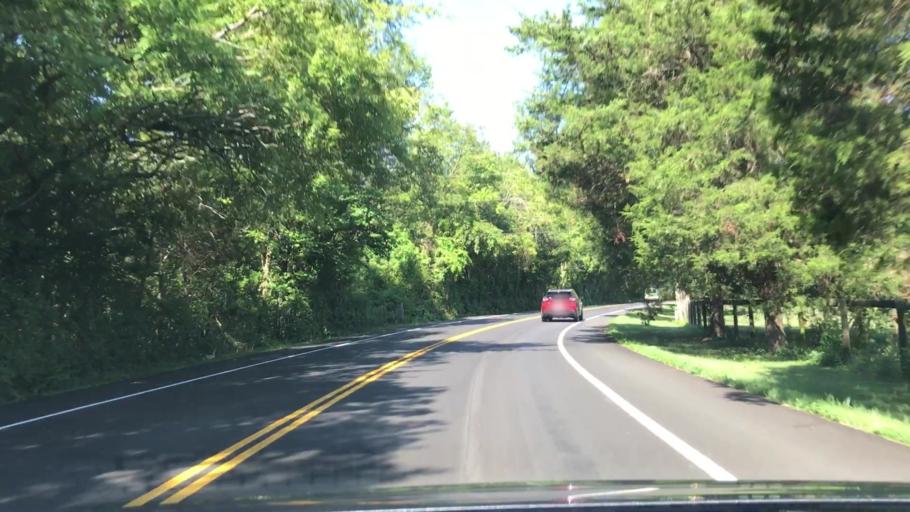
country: US
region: Tennessee
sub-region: Williamson County
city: Franklin
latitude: 35.9721
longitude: -86.8644
